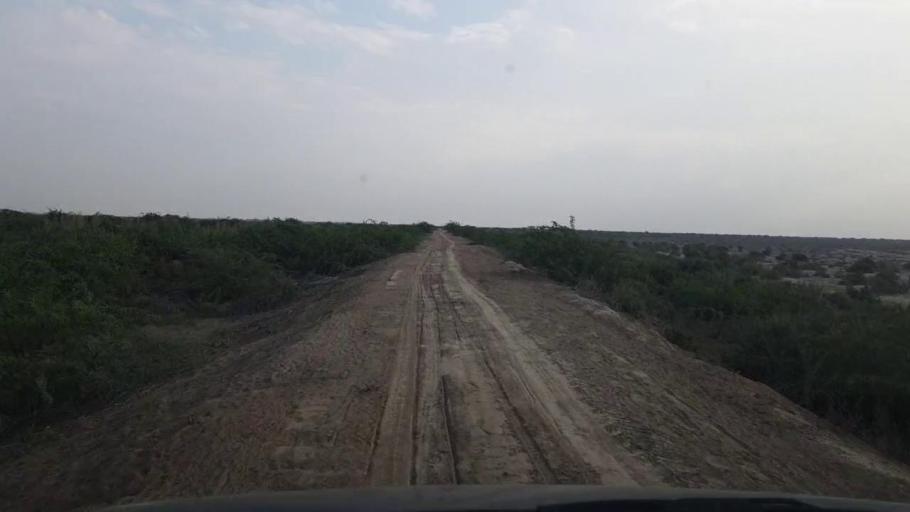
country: PK
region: Sindh
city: Badin
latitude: 24.4804
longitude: 68.6987
